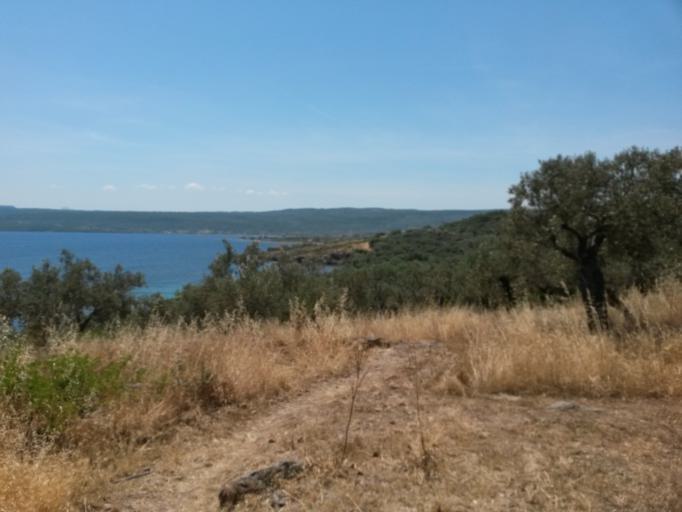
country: GR
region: North Aegean
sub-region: Nomos Lesvou
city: Mantamados
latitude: 39.2991
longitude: 26.3941
